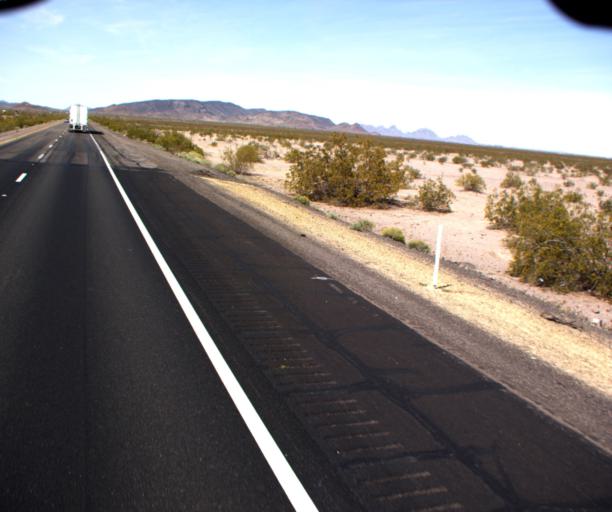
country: US
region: Arizona
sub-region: La Paz County
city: Salome
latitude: 33.6397
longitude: -113.8253
